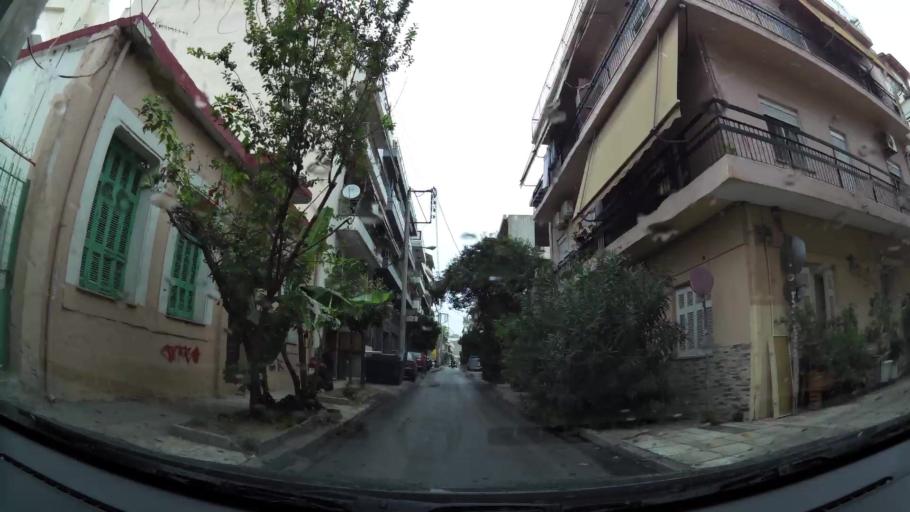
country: GR
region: Attica
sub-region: Nomos Piraios
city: Nikaia
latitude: 37.9621
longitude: 23.6497
